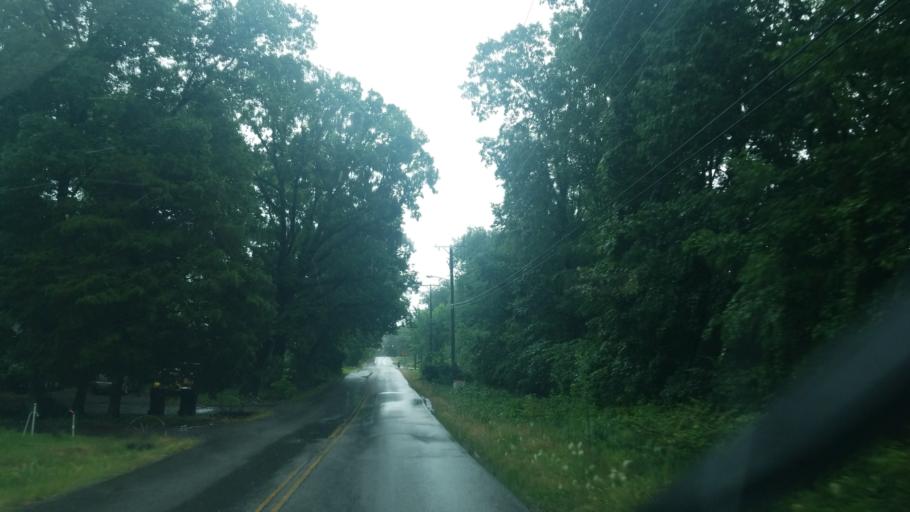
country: US
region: Tennessee
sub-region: Rutherford County
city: La Vergne
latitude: 36.0496
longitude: -86.6026
